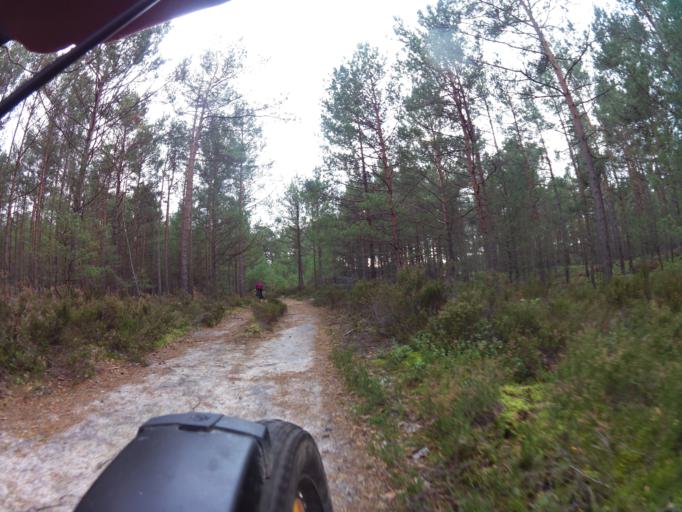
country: PL
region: Pomeranian Voivodeship
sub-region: Powiat pucki
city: Hel
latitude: 54.6271
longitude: 18.8026
